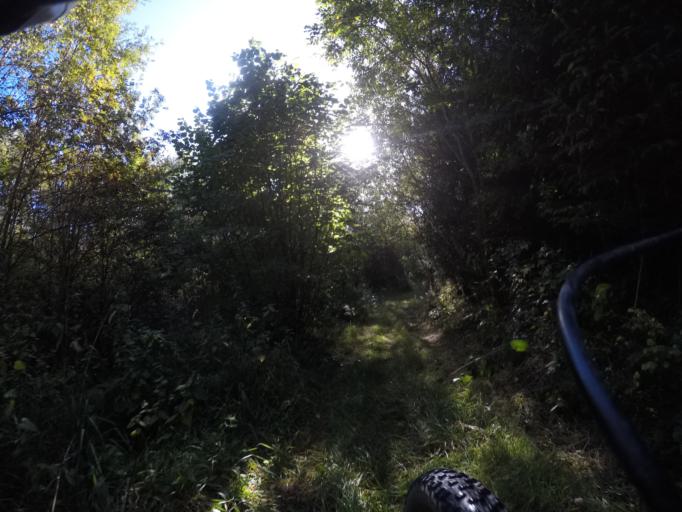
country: BE
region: Wallonia
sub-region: Province du Luxembourg
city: Fauvillers
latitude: 49.9032
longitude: 5.6737
